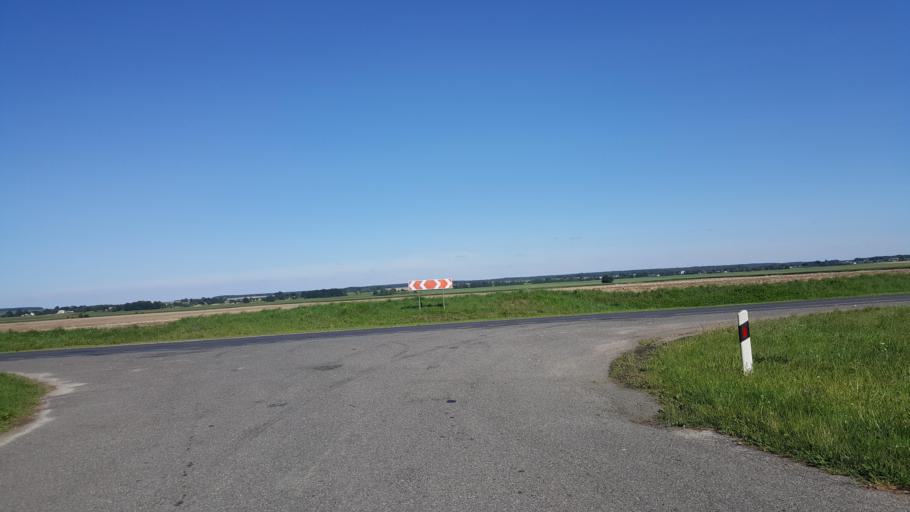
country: BY
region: Brest
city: Charnawchytsy
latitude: 52.2388
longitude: 23.7461
